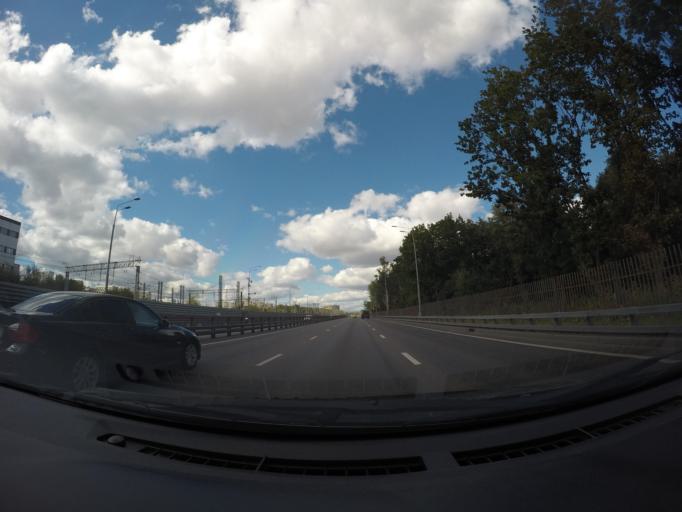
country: RU
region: Moscow
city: Perovo
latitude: 55.7271
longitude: 37.7864
